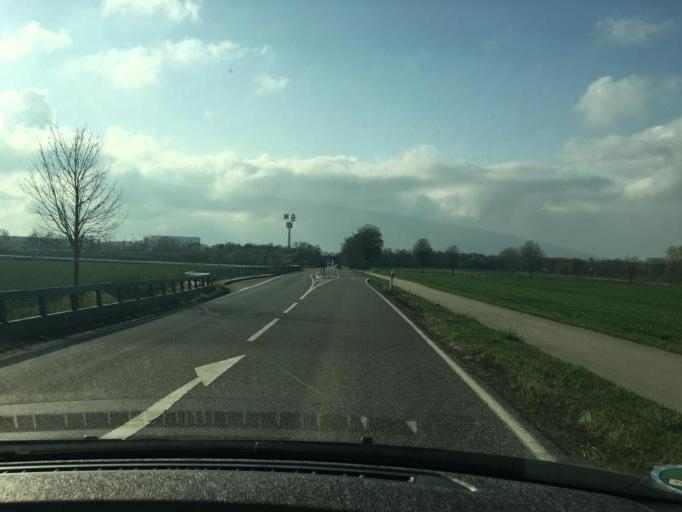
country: DE
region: North Rhine-Westphalia
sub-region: Regierungsbezirk Koln
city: Weilerswist
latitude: 50.7459
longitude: 6.8684
